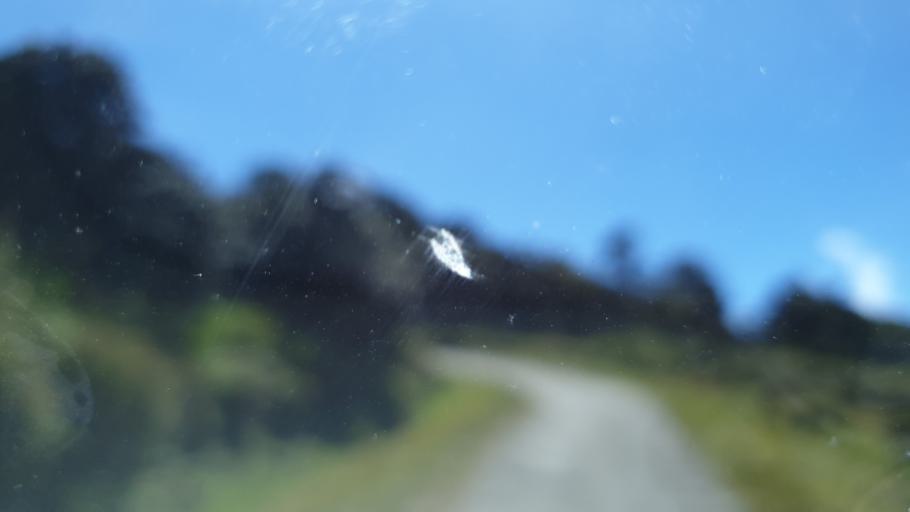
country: LK
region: Uva
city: Haputale
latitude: 6.7987
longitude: 80.8135
